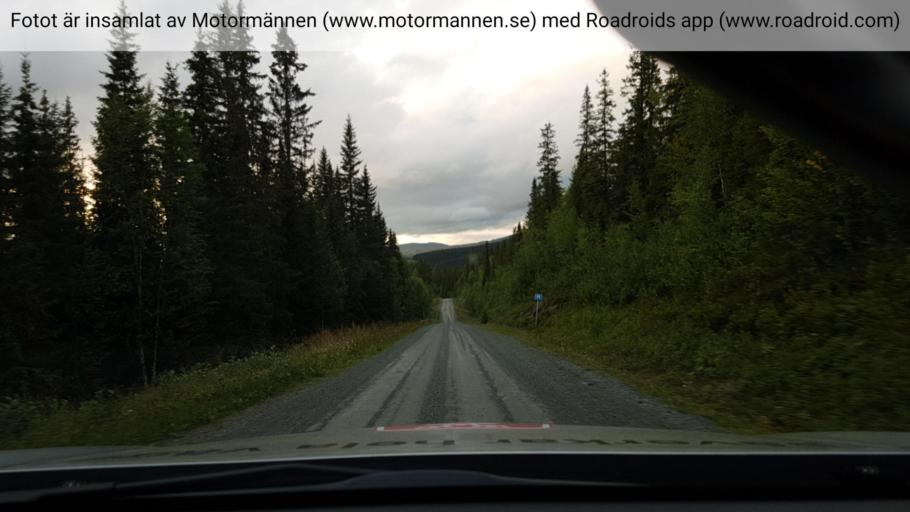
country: SE
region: Vaesterbotten
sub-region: Vilhelmina Kommun
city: Sjoberg
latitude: 65.4980
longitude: 15.4865
